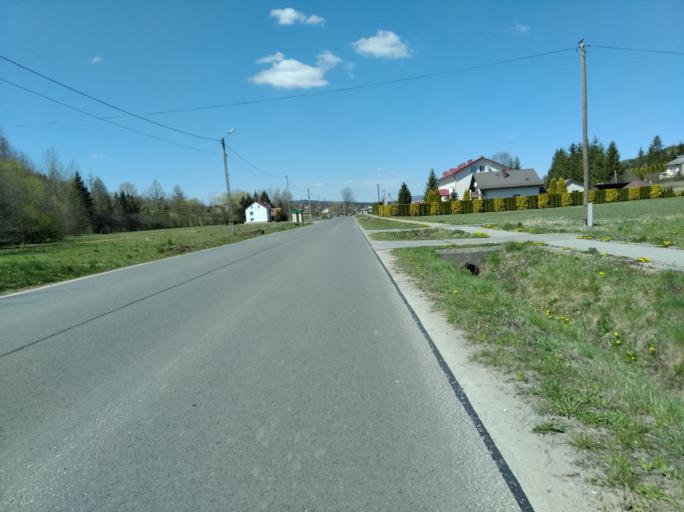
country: PL
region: Subcarpathian Voivodeship
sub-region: Powiat brzozowski
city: Dydnia
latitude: 49.6864
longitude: 22.1713
